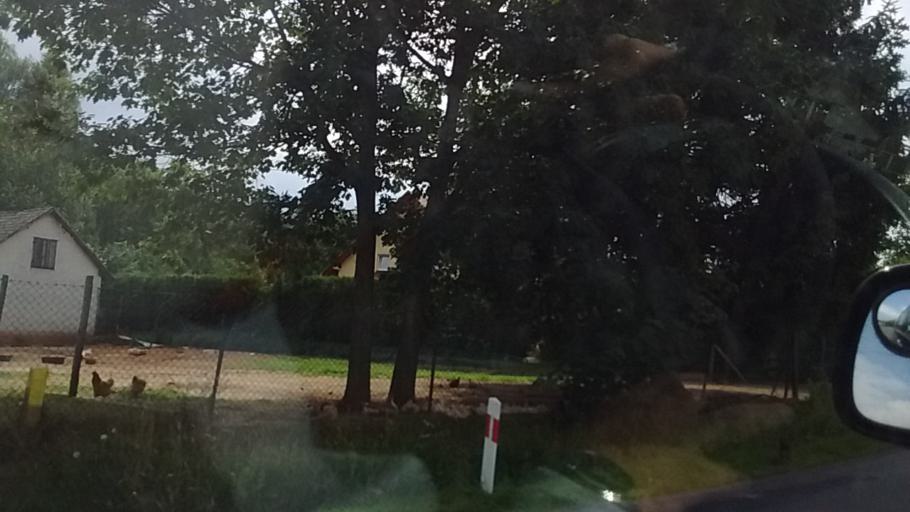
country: PL
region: Subcarpathian Voivodeship
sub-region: Powiat lancucki
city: Zolynia
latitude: 50.1942
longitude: 22.3391
